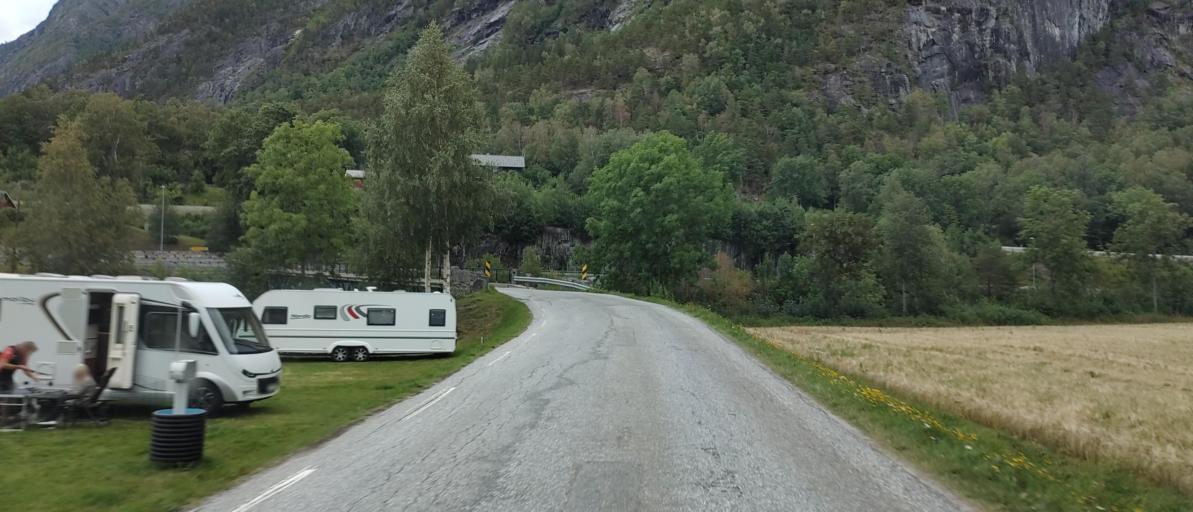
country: NO
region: More og Romsdal
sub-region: Rauma
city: Andalsnes
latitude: 62.5318
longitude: 7.7368
